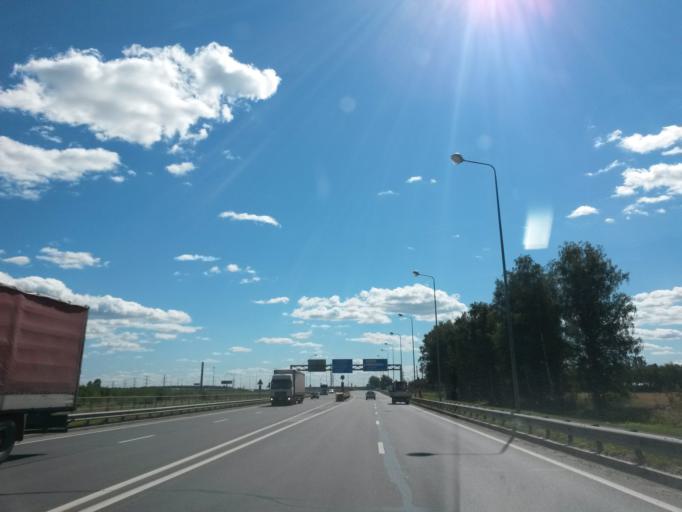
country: RU
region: Jaroslavl
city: Yaroslavl
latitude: 57.6931
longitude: 39.8985
